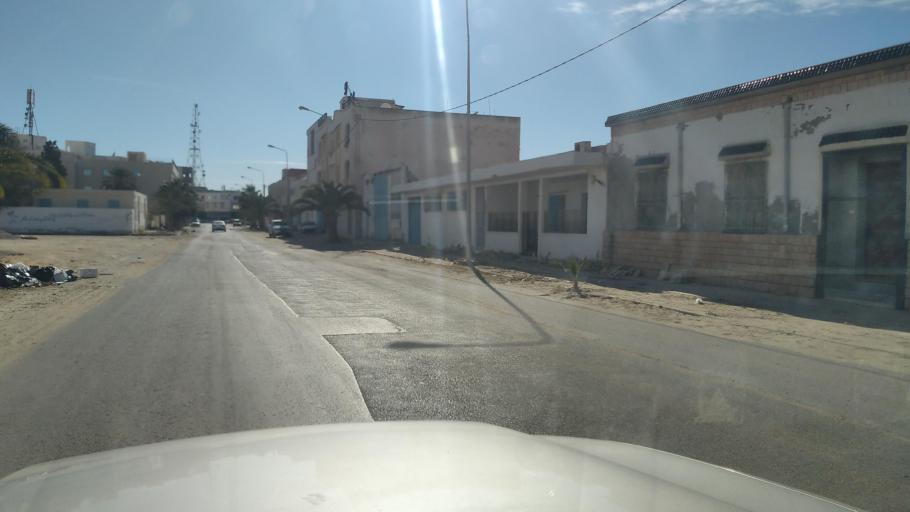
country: TN
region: Qabis
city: Gabes
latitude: 33.8907
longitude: 10.1110
